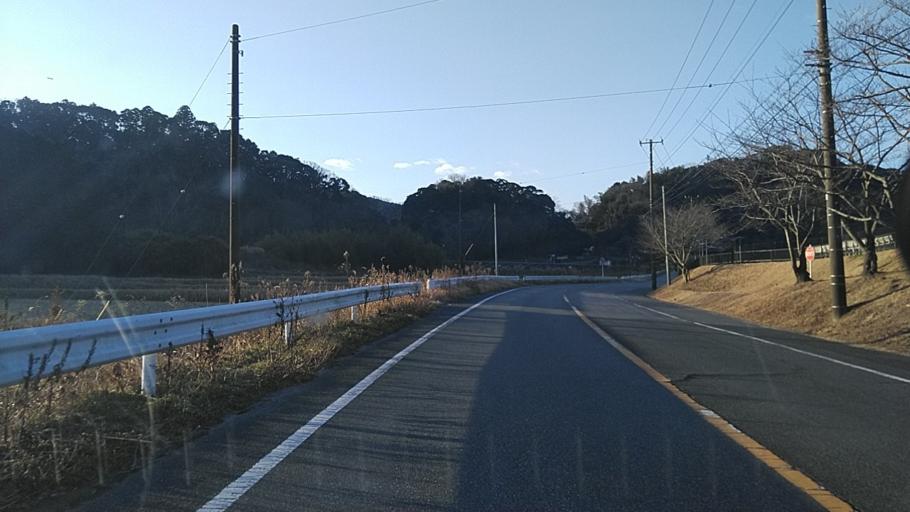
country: JP
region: Chiba
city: Kimitsu
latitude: 35.2732
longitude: 139.9212
